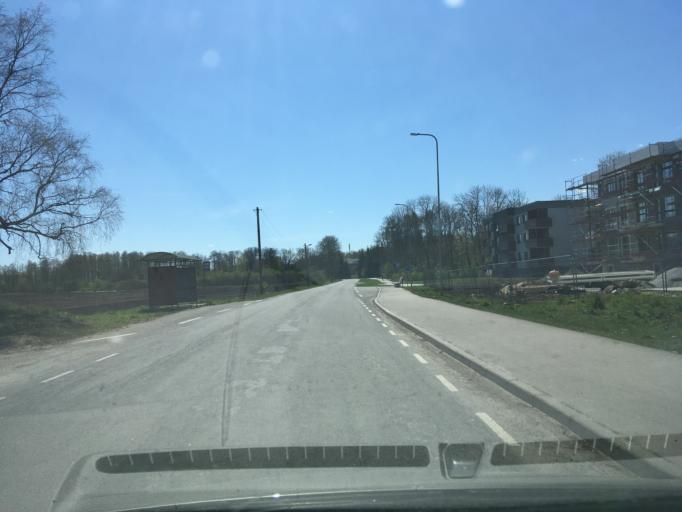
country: EE
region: Harju
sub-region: Raasiku vald
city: Arukula
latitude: 59.3632
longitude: 25.0827
